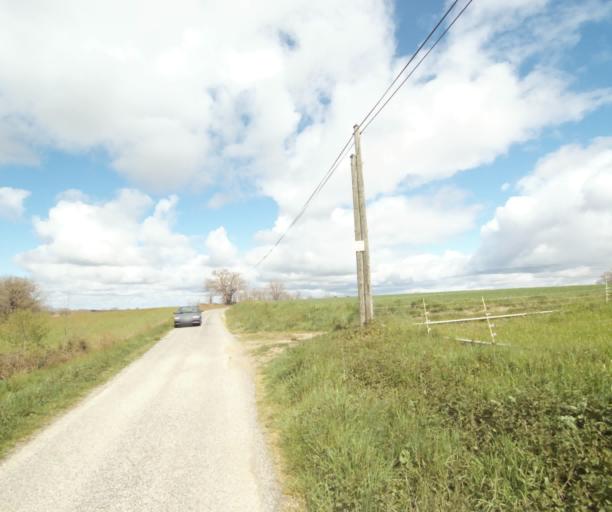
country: FR
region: Midi-Pyrenees
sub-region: Departement de l'Ariege
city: Saverdun
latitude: 43.2075
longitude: 1.5832
